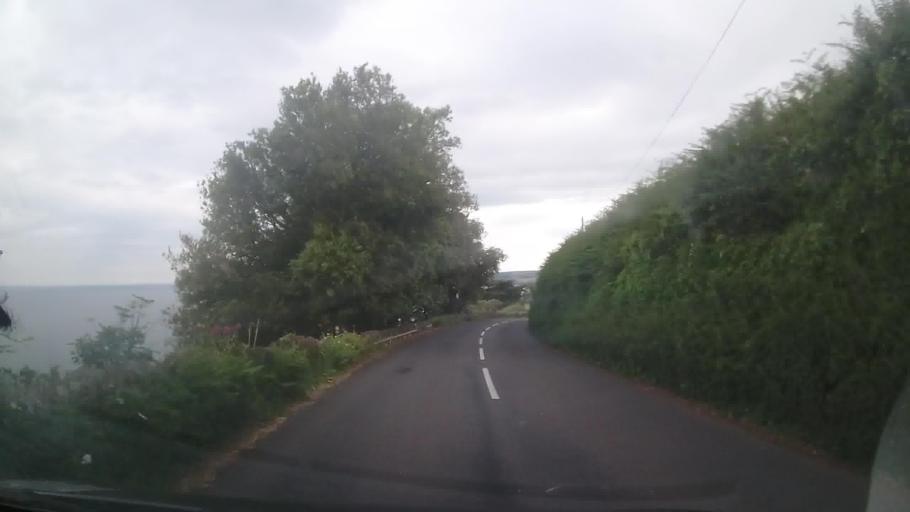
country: GB
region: England
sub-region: Devon
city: Dartmouth
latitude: 50.3047
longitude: -3.6339
